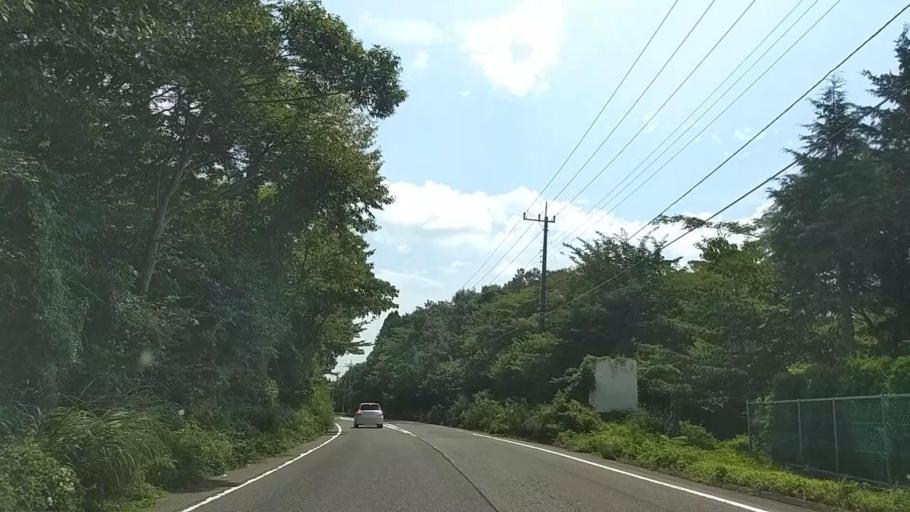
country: JP
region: Shizuoka
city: Fujinomiya
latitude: 35.3593
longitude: 138.5776
